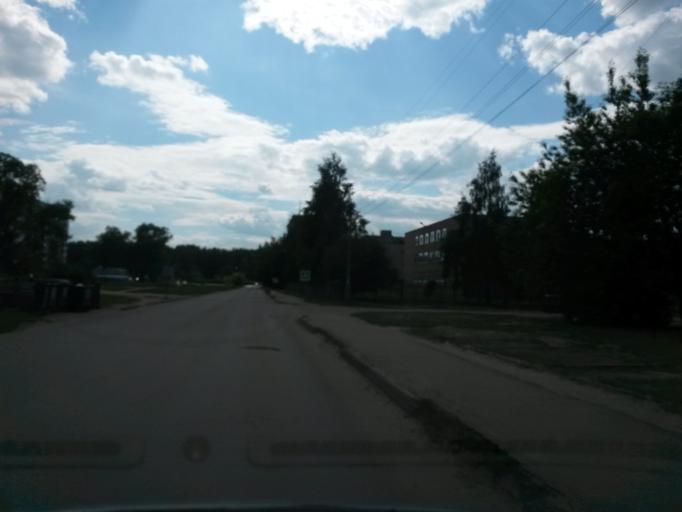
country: RU
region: Jaroslavl
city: Yaroslavl
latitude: 57.6446
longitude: 39.9478
